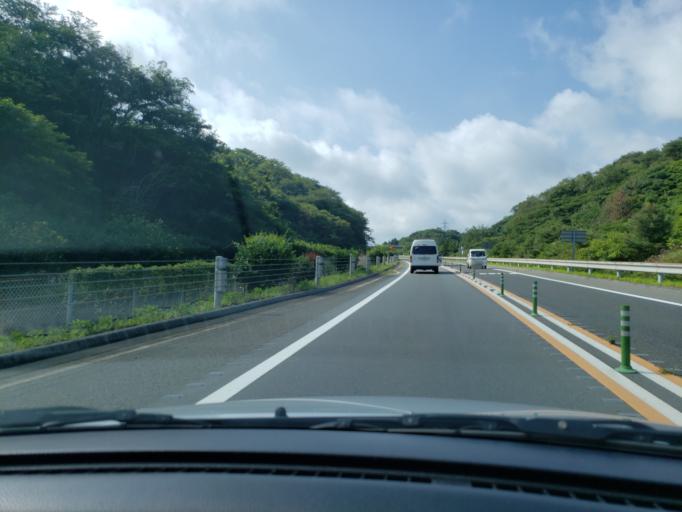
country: JP
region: Hiroshima
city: Onomichi
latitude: 34.3693
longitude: 133.1905
